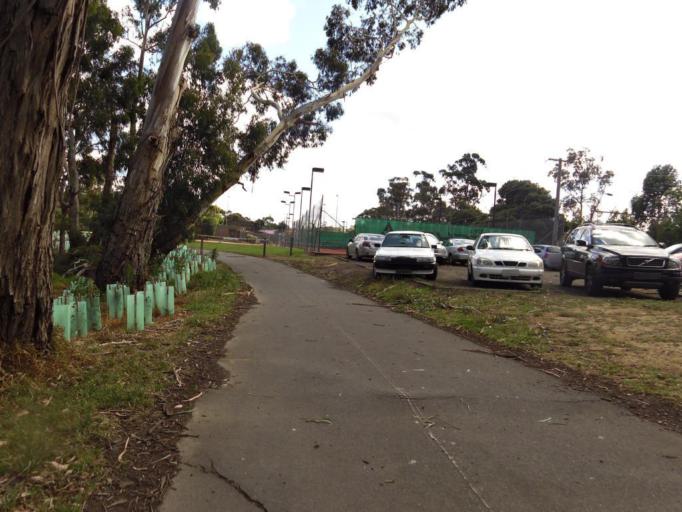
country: AU
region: Victoria
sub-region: Nillumbik
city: Eltham North
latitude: -37.7140
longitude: 145.1461
